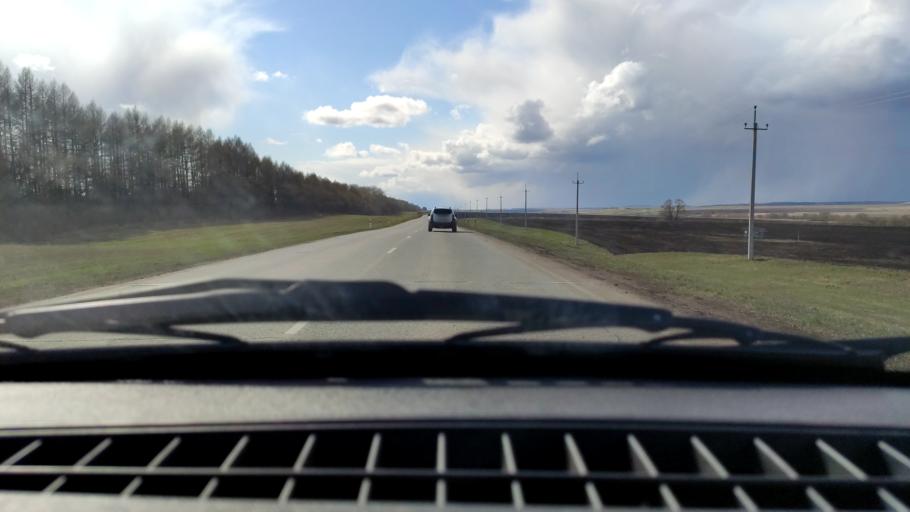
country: RU
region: Bashkortostan
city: Chekmagush
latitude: 55.1118
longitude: 54.9100
